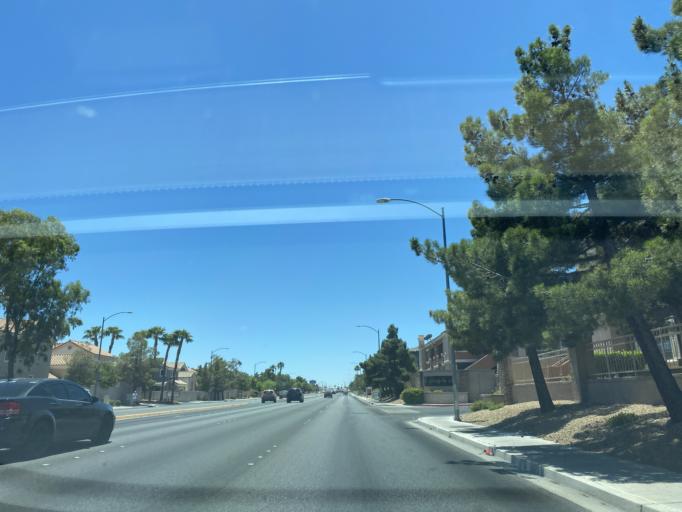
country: US
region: Nevada
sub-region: Clark County
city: Spring Valley
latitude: 36.1869
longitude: -115.2601
